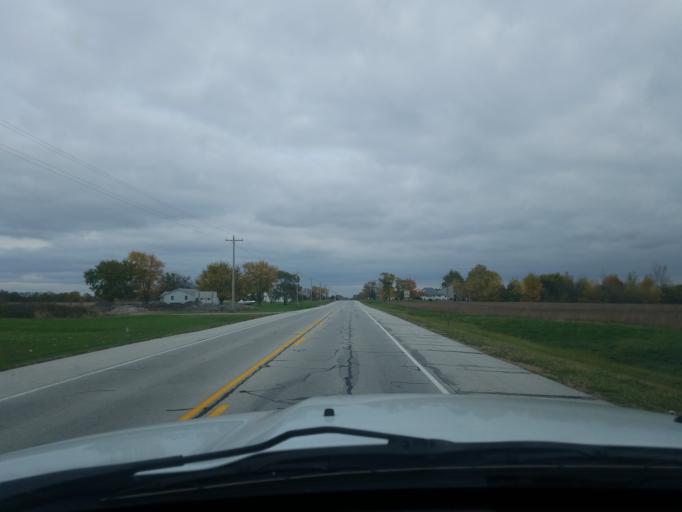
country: US
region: Indiana
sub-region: Johnson County
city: Franklin
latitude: 39.4954
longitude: -85.9215
